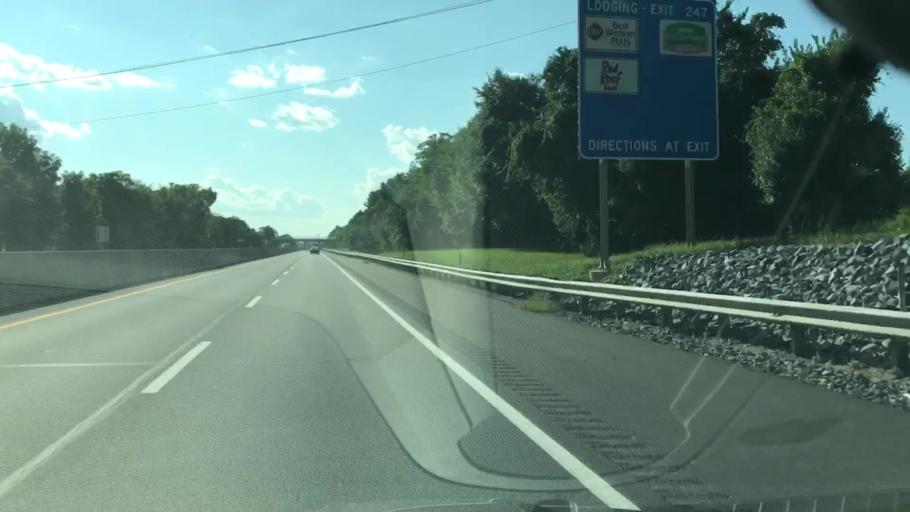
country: US
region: Pennsylvania
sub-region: Dauphin County
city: Highspire
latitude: 40.2124
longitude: -76.7643
